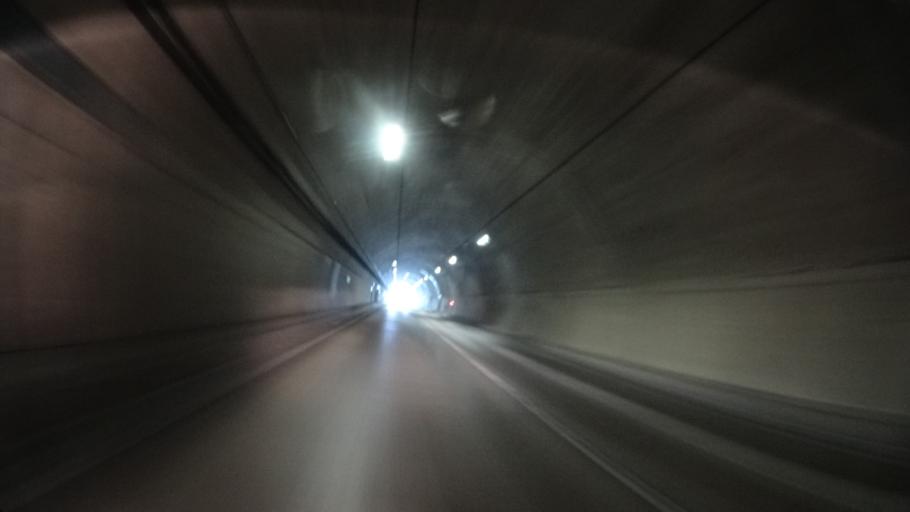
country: JP
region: Fukui
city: Maruoka
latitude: 36.1351
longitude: 136.3245
